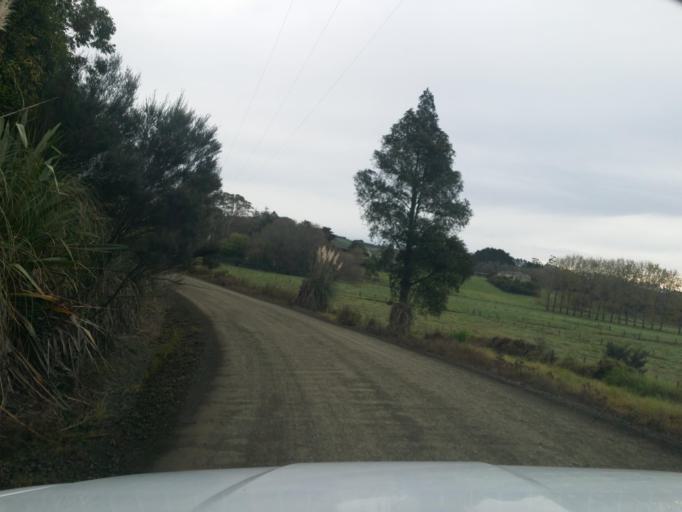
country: NZ
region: Northland
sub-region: Whangarei
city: Maungatapere
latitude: -35.8192
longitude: 174.0403
